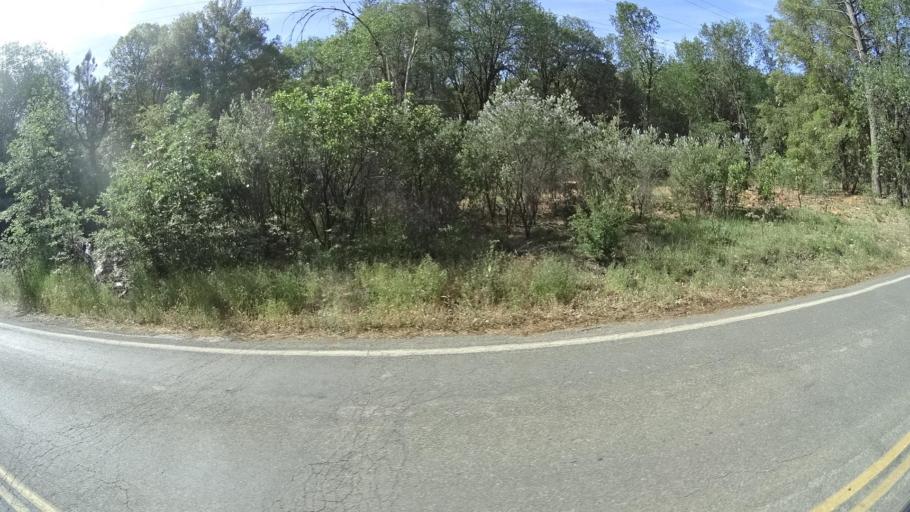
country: US
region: California
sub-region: Lake County
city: Soda Bay
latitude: 38.9113
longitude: -122.7633
